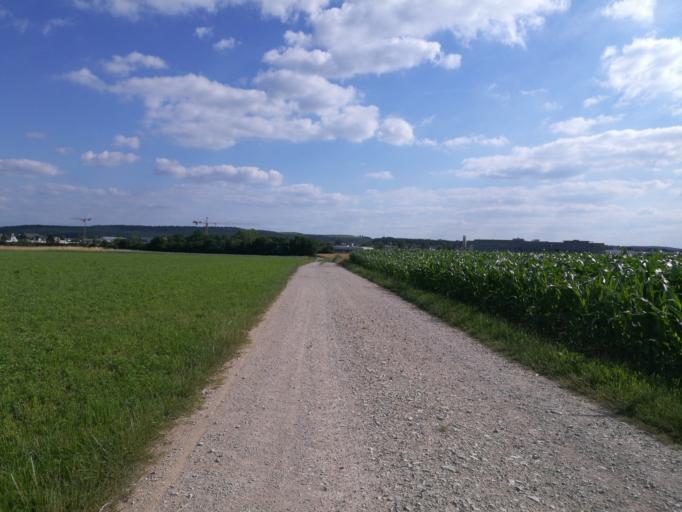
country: DE
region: Bavaria
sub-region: Regierungsbezirk Mittelfranken
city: Veitsbronn
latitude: 49.4993
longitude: 10.9182
